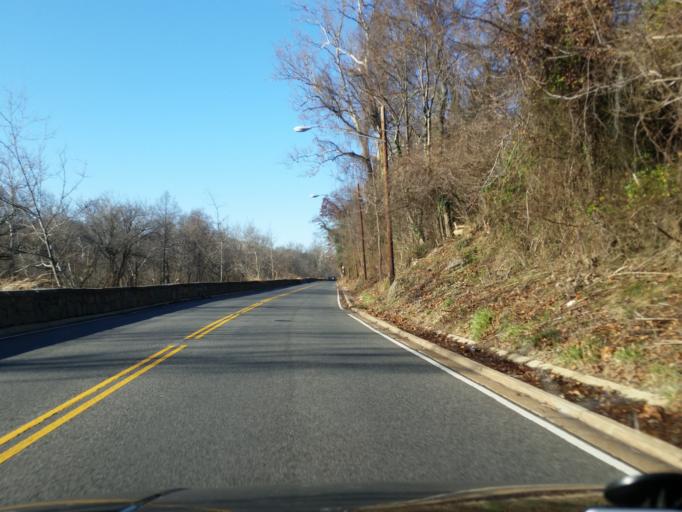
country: US
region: Virginia
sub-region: Arlington County
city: Arlington
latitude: 38.9093
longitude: -77.0932
